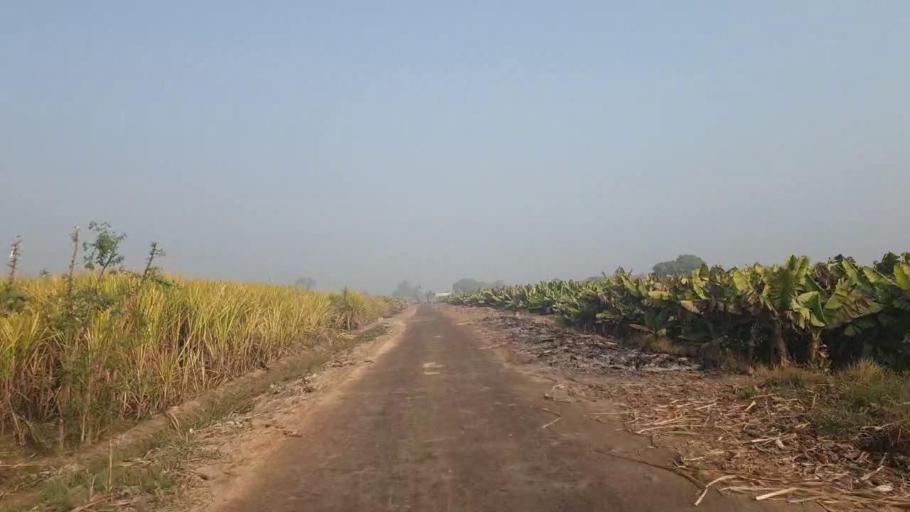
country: PK
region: Sindh
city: Tando Adam
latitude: 25.7976
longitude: 68.6153
